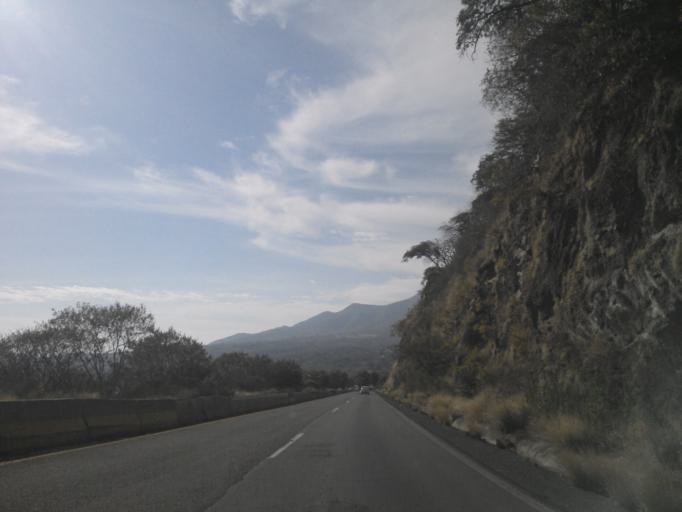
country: MX
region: Jalisco
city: Ixtlahuacan de los Membrillos
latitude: 20.3272
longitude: -103.1849
